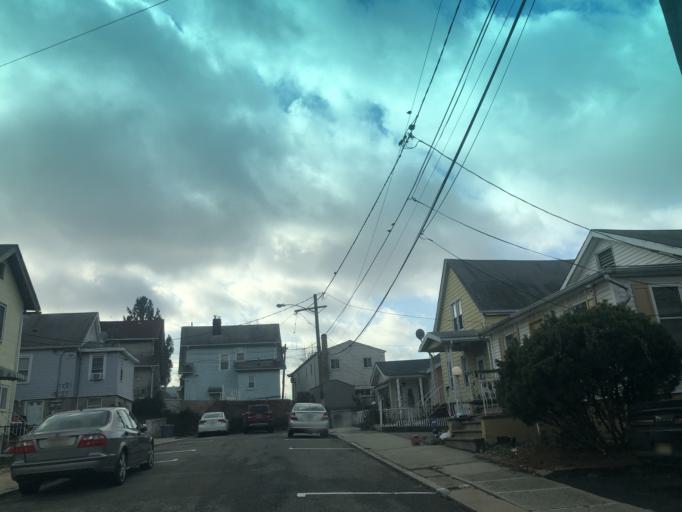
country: US
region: New Jersey
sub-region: Hudson County
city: Union City
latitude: 40.7862
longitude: -74.0332
